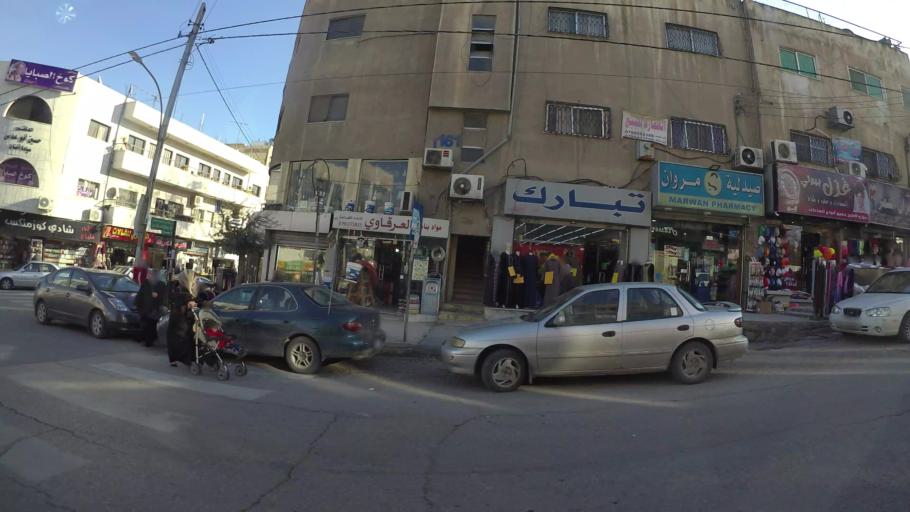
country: JO
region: Amman
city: Amman
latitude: 31.9706
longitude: 35.9548
